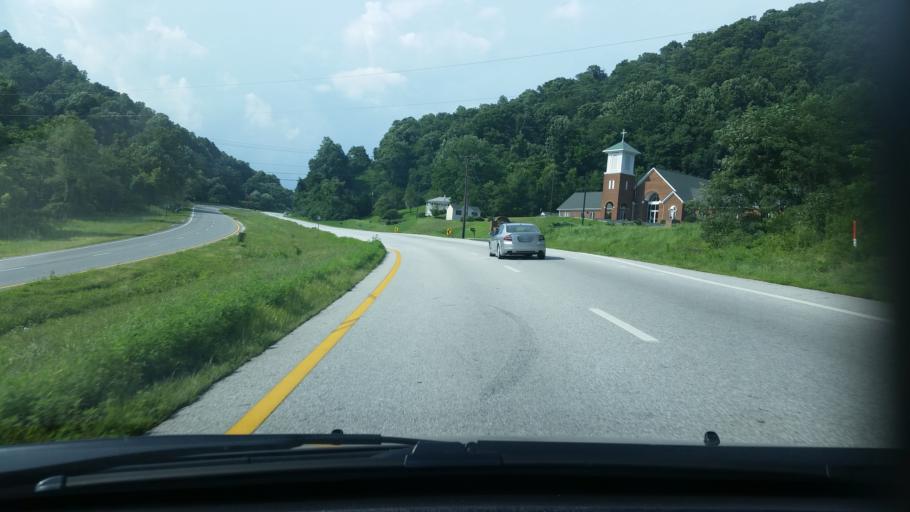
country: US
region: Virginia
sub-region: Nelson County
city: Lovingston
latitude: 37.7681
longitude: -78.8694
